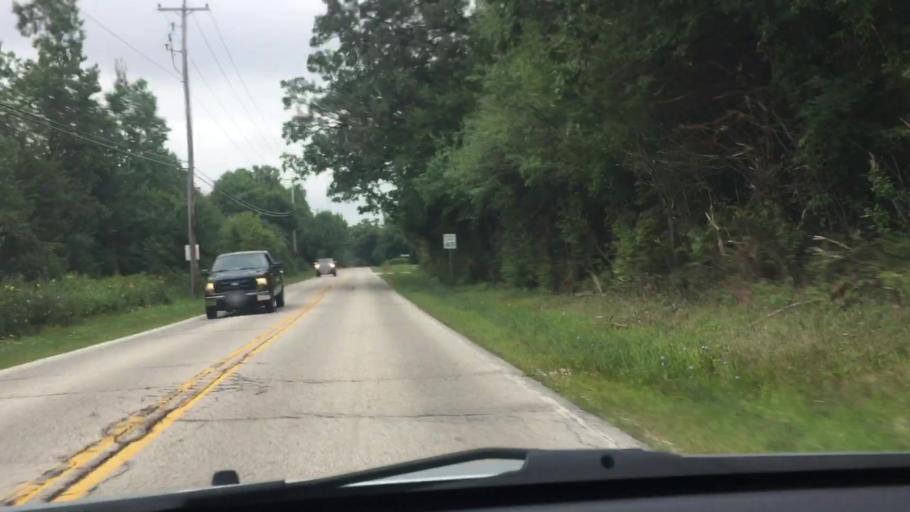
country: US
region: Wisconsin
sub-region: Waukesha County
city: Dousman
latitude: 43.0299
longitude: -88.4427
